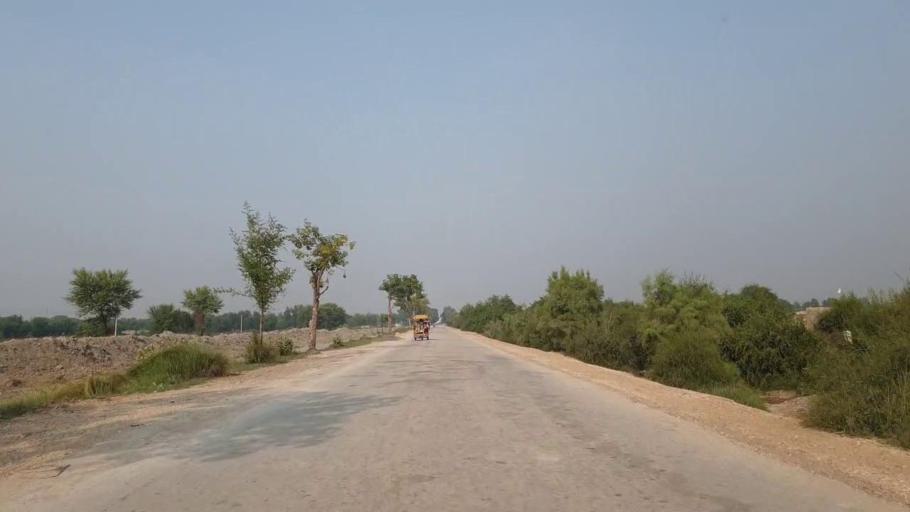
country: PK
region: Sindh
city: Bhan
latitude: 26.5820
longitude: 67.7286
